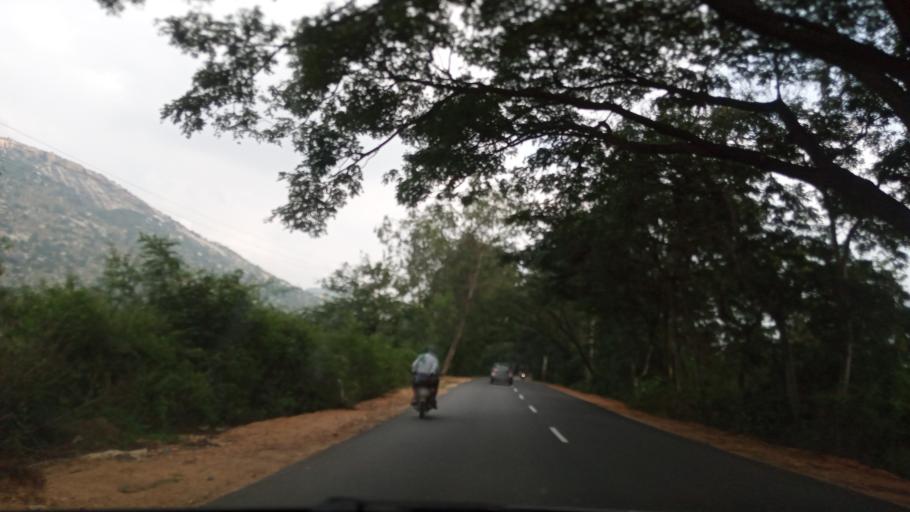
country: IN
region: Andhra Pradesh
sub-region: Chittoor
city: Madanapalle
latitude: 13.6368
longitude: 78.5808
